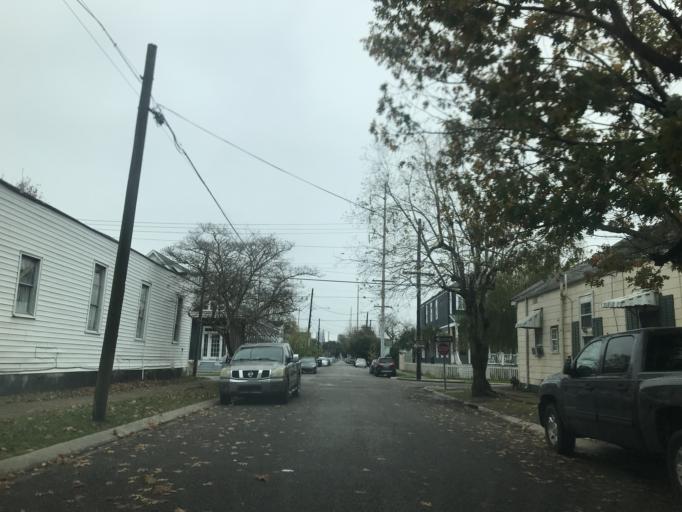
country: US
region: Louisiana
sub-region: Orleans Parish
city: New Orleans
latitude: 29.9698
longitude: -90.1020
